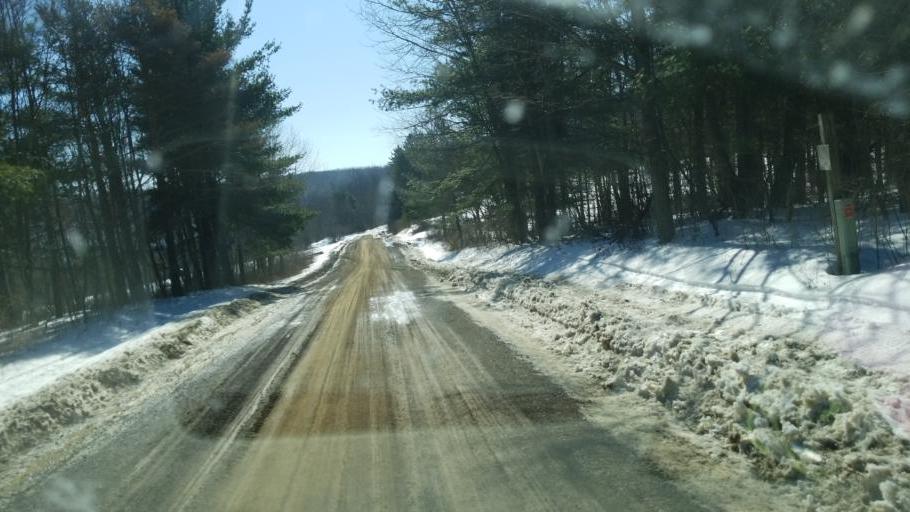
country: US
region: New York
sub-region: Allegany County
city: Alfred
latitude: 42.2493
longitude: -77.7318
